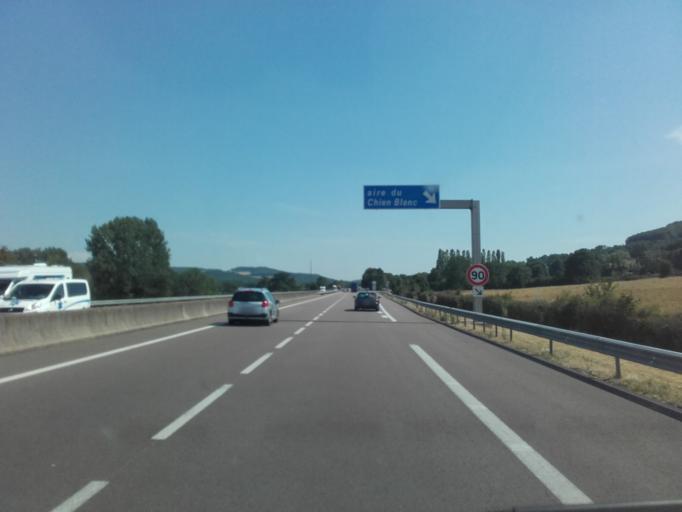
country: FR
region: Bourgogne
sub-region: Departement de la Cote-d'Or
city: Pouilly-en-Auxois
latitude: 47.3210
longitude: 4.4909
